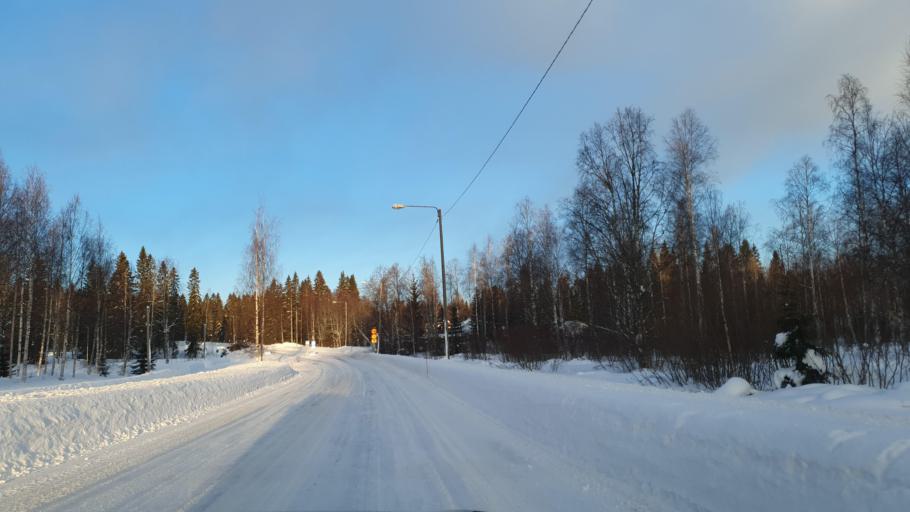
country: FI
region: Kainuu
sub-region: Kajaani
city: Ristijaervi
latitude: 64.3385
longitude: 28.1069
